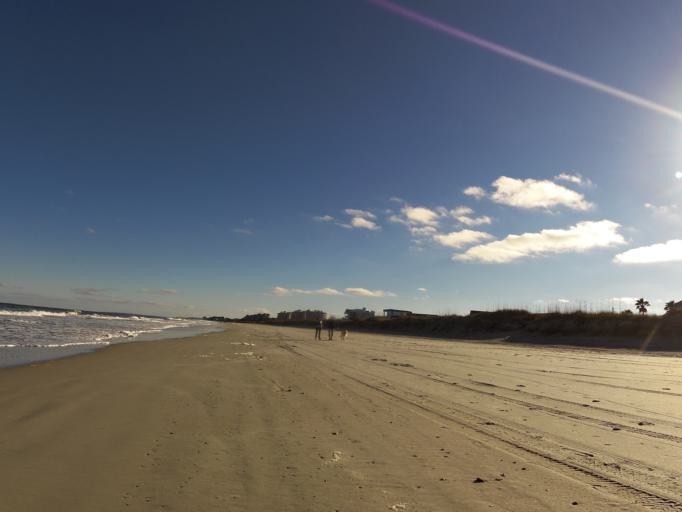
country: US
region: Florida
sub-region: Nassau County
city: Fernandina Beach
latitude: 30.5730
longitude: -81.4431
